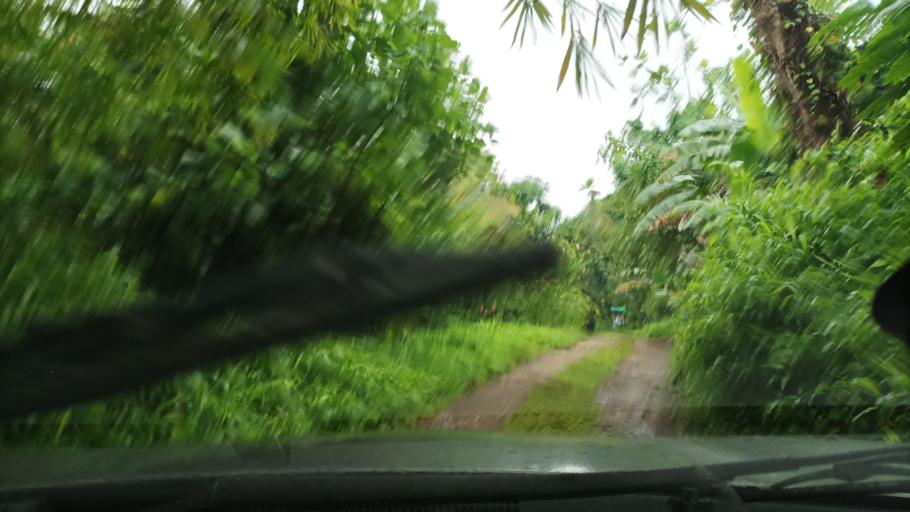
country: FM
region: Pohnpei
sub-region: Sokehs Municipality
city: Palikir - National Government Center
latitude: 6.8558
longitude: 158.1857
